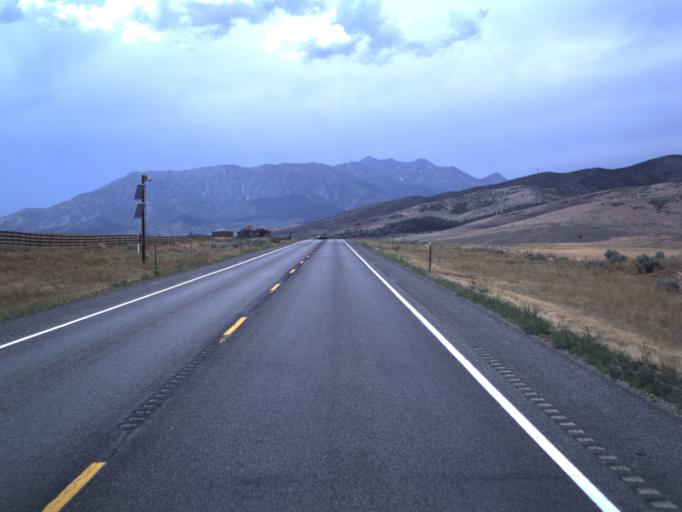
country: US
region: Utah
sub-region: Sanpete County
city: Fountain Green
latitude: 39.6723
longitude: -111.6645
